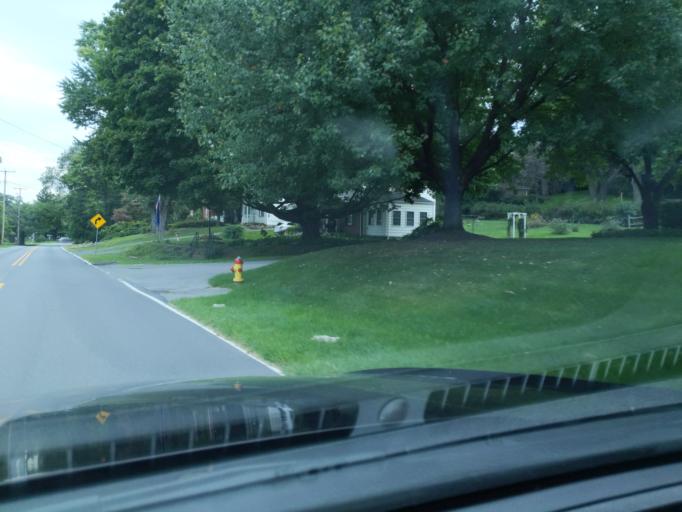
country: US
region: Pennsylvania
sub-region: Blair County
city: Lakemont
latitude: 40.4774
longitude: -78.4104
